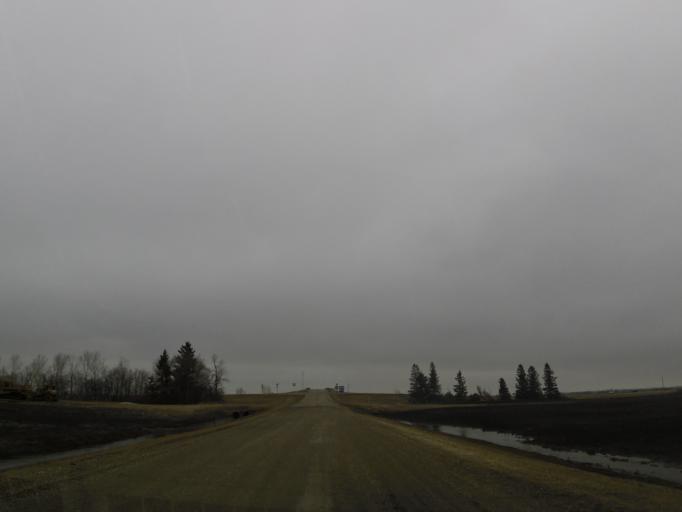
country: US
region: North Dakota
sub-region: Walsh County
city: Grafton
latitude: 48.3532
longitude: -97.1939
